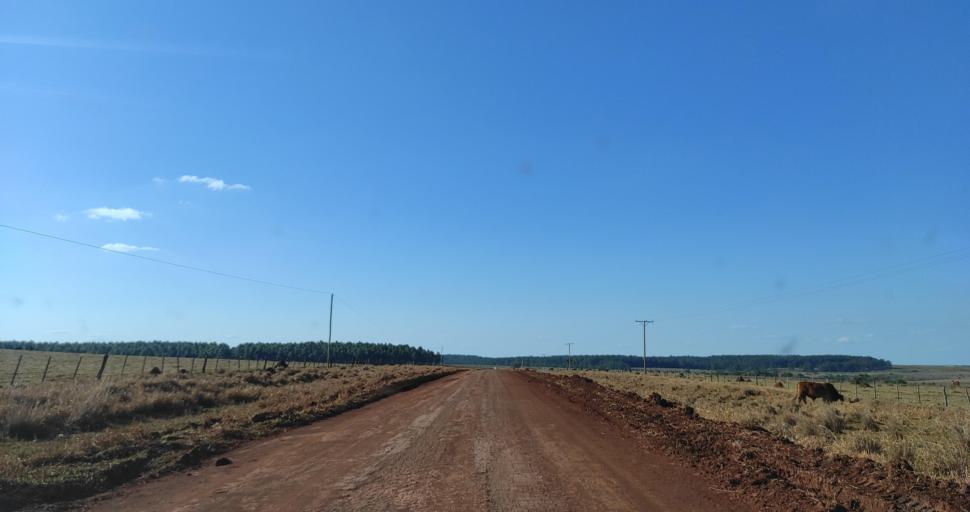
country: PY
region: Itapua
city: San Juan del Parana
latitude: -27.4292
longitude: -56.0833
